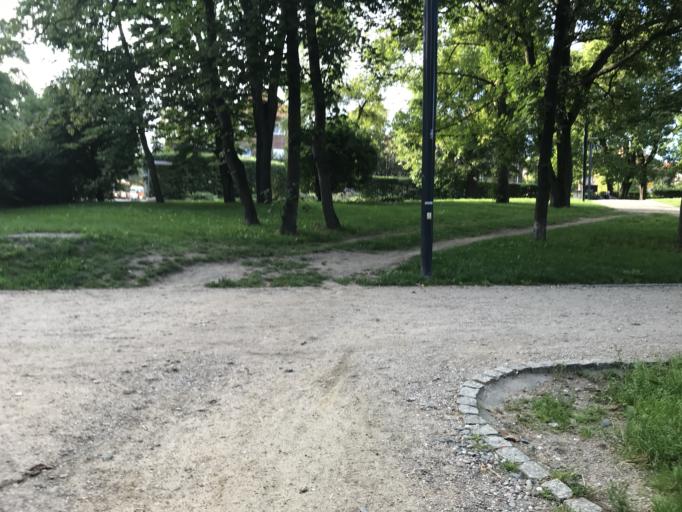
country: PL
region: Pomeranian Voivodeship
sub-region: Gdansk
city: Gdansk
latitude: 54.3533
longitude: 18.6345
